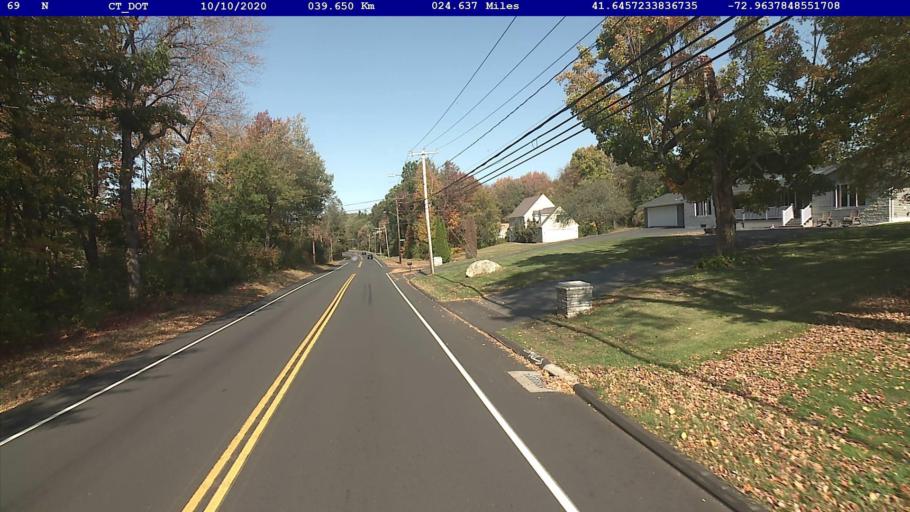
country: US
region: Connecticut
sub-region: Hartford County
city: Bristol
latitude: 41.6457
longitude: -72.9638
